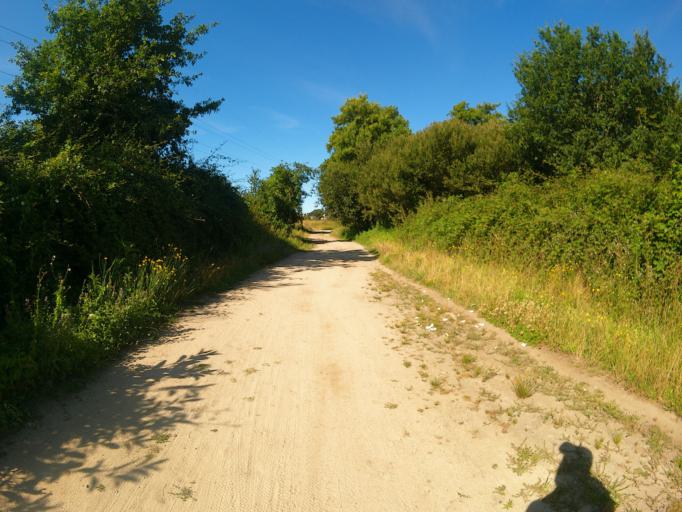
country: PT
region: Viana do Castelo
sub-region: Ponte de Lima
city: Ponte de Lima
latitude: 41.7391
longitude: -8.6455
